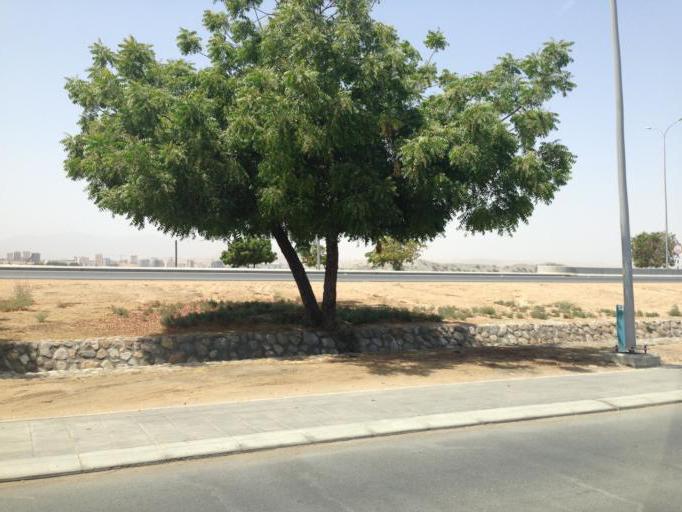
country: OM
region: Muhafazat Masqat
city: Bawshar
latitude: 23.6031
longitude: 58.3444
